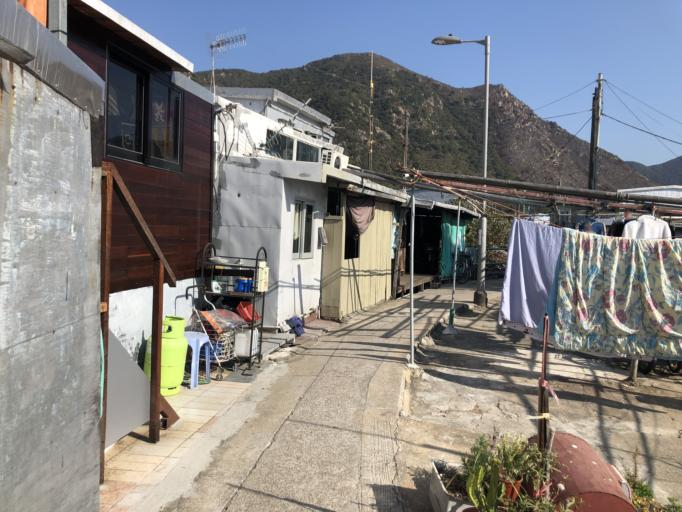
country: HK
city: Tai O
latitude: 22.2556
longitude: 113.8654
